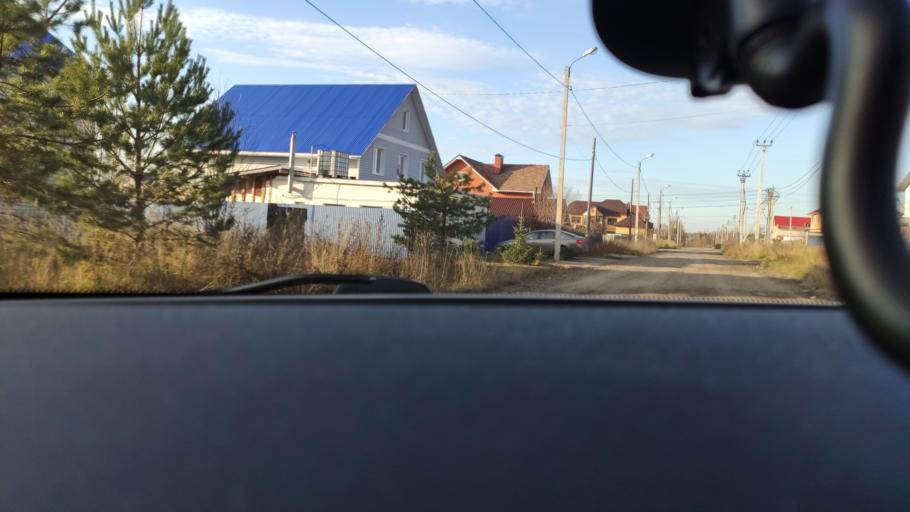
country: RU
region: Perm
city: Kondratovo
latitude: 58.0587
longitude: 56.0364
